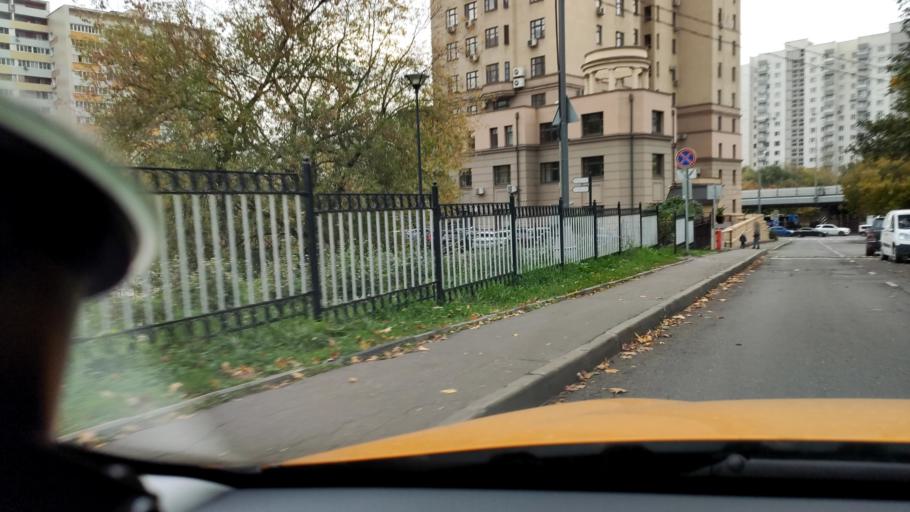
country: RU
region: Moskovskaya
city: Bol'shaya Setun'
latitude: 55.7195
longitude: 37.4139
